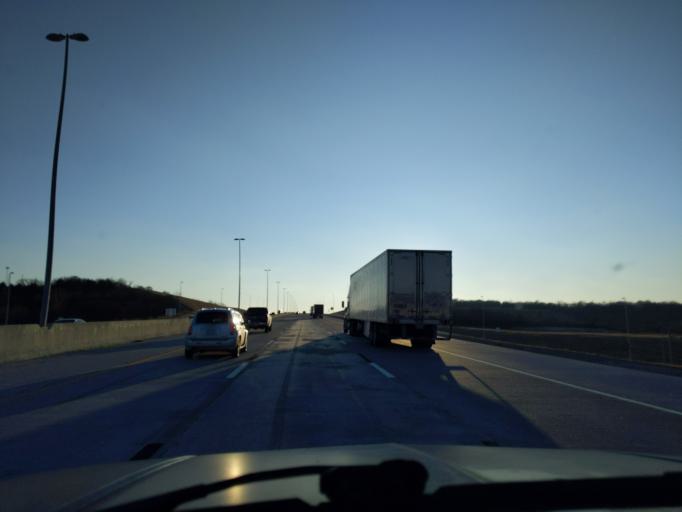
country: US
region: Oklahoma
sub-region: Creek County
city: Kellyville
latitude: 35.9872
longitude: -96.1948
